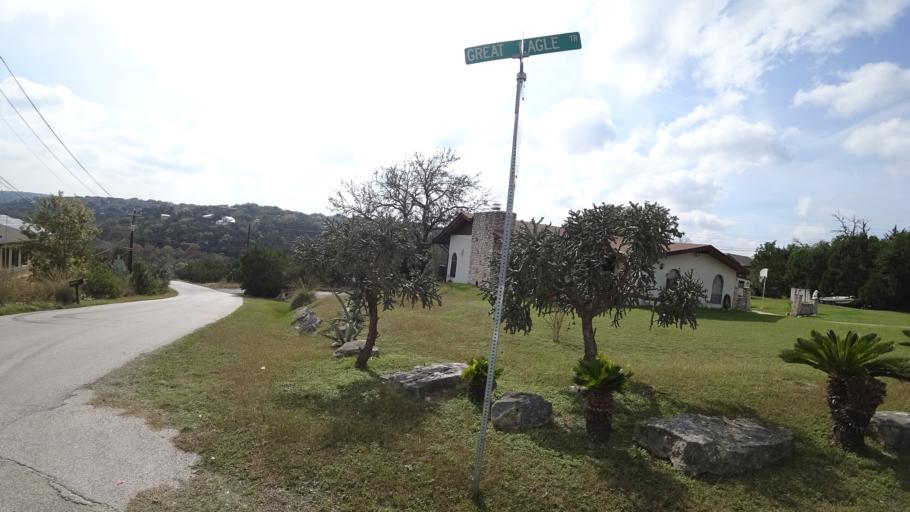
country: US
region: Texas
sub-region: Travis County
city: Hudson Bend
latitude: 30.3833
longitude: -97.9226
